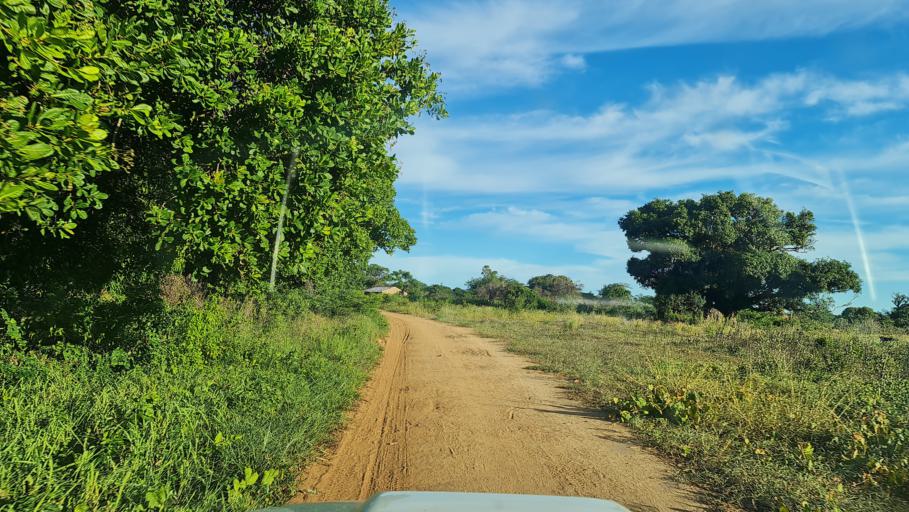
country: MZ
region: Nampula
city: Antonio Enes
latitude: -15.6742
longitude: 40.3016
